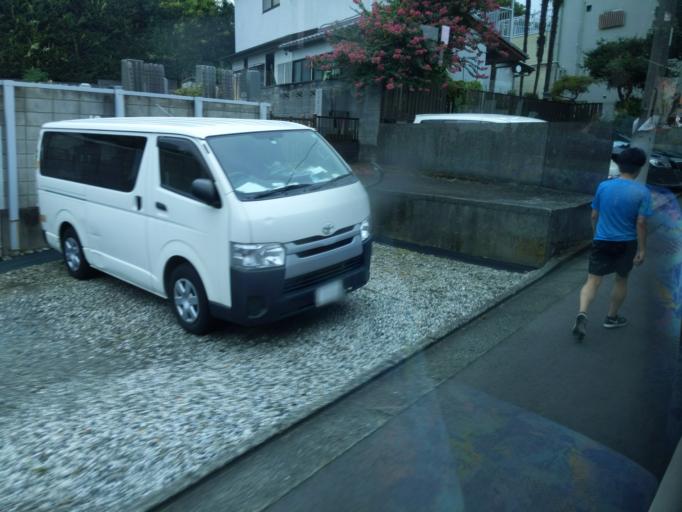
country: JP
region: Kanagawa
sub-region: Kawasaki-shi
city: Kawasaki
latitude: 35.5857
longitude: 139.6948
